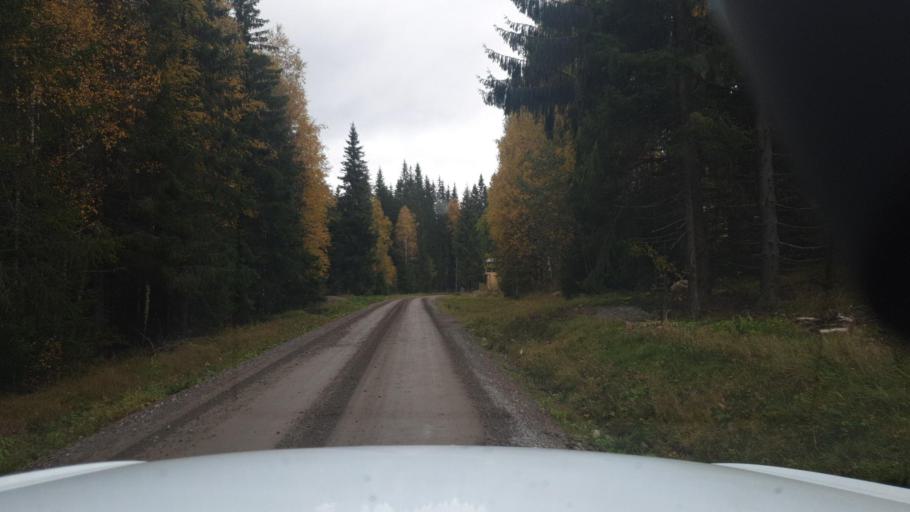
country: SE
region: Vaermland
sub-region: Eda Kommun
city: Charlottenberg
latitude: 60.0356
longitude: 12.5939
